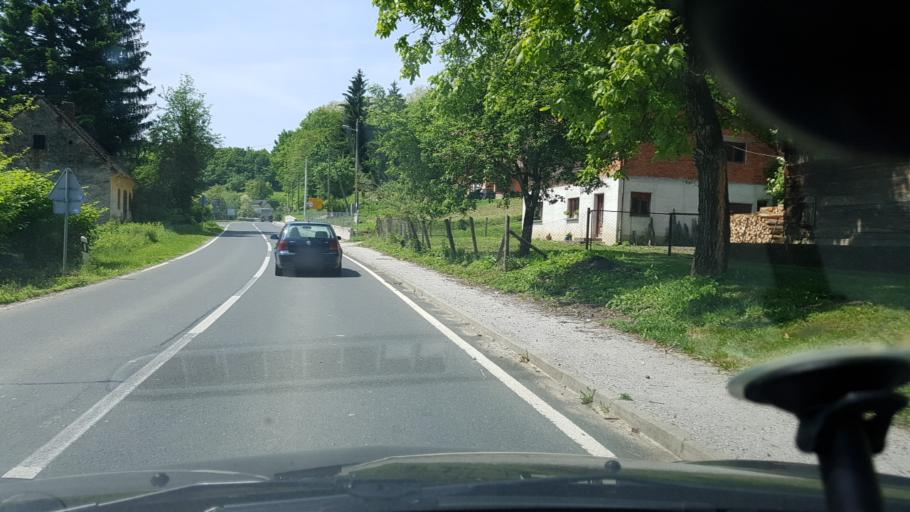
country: HR
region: Krapinsko-Zagorska
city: Marija Bistrica
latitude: 45.9856
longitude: 16.1150
